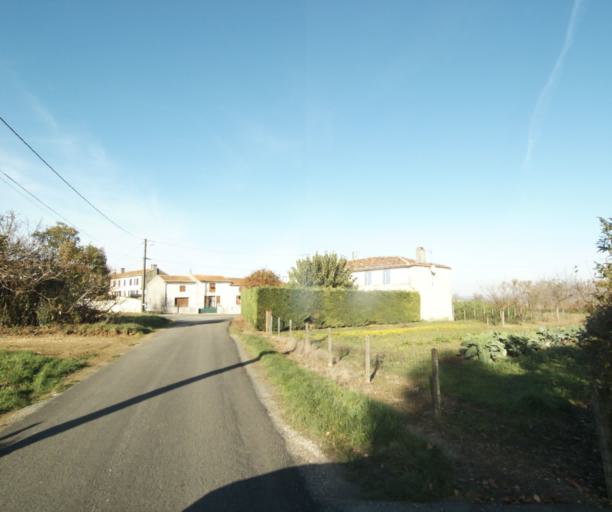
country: FR
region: Poitou-Charentes
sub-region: Departement de la Charente-Maritime
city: Burie
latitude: 45.7786
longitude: -0.4330
